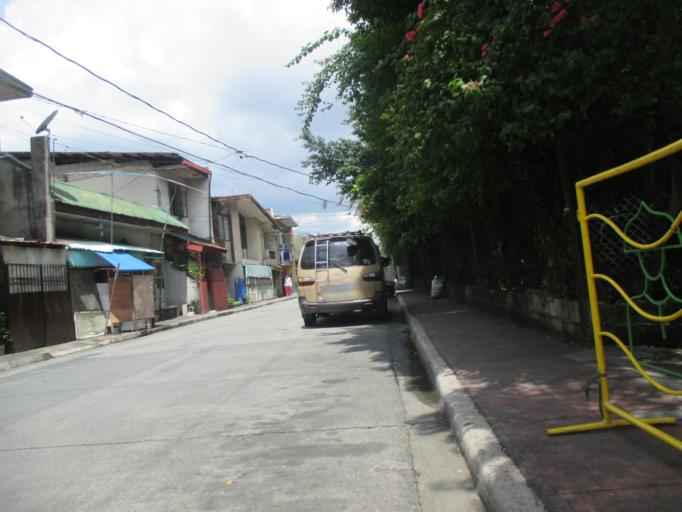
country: PH
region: Metro Manila
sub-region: Marikina
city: Calumpang
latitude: 14.6303
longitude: 121.0975
